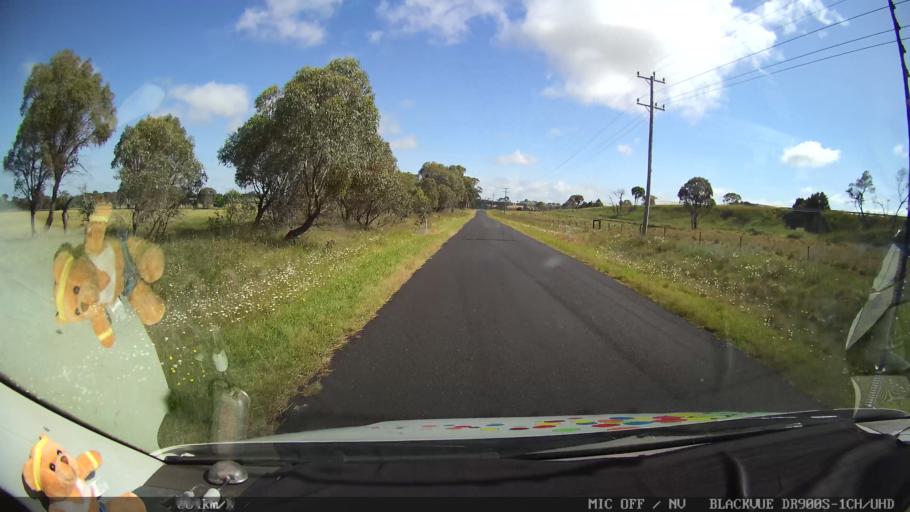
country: AU
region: New South Wales
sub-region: Guyra
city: Guyra
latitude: -30.1960
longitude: 151.6759
